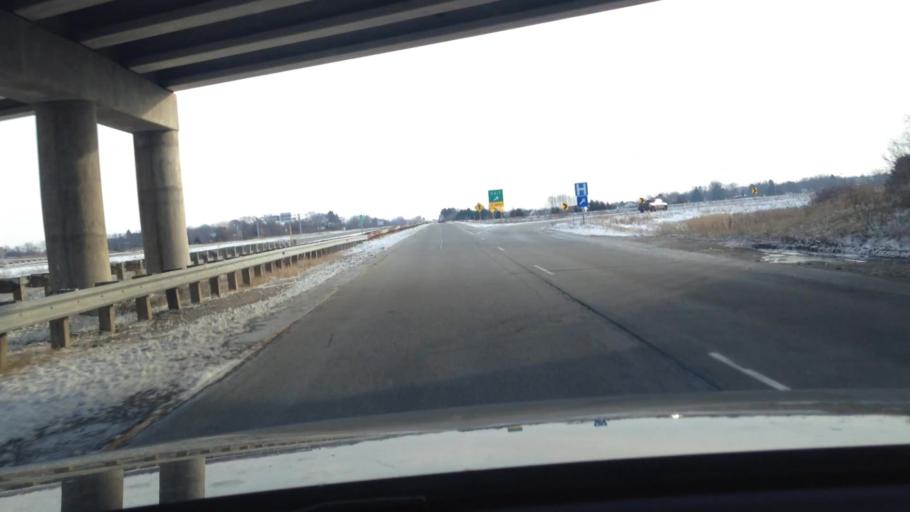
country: US
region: Wisconsin
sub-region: Walworth County
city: Elkhorn
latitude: 42.6699
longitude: -88.5190
